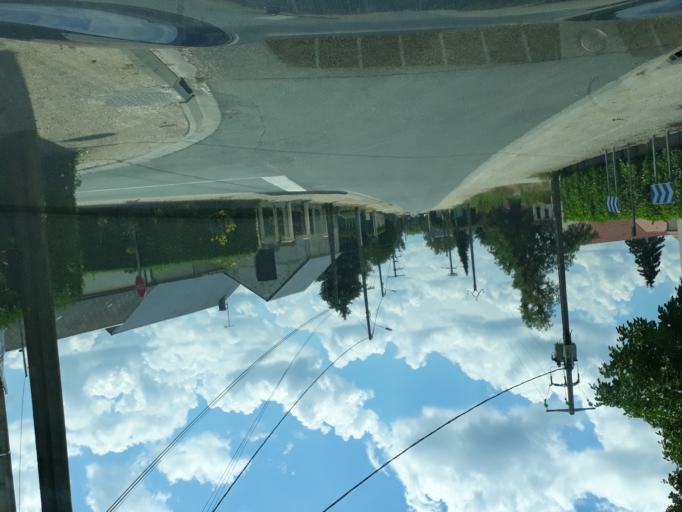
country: FR
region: Centre
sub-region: Departement du Loiret
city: Chevilly
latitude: 48.0324
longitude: 1.9137
